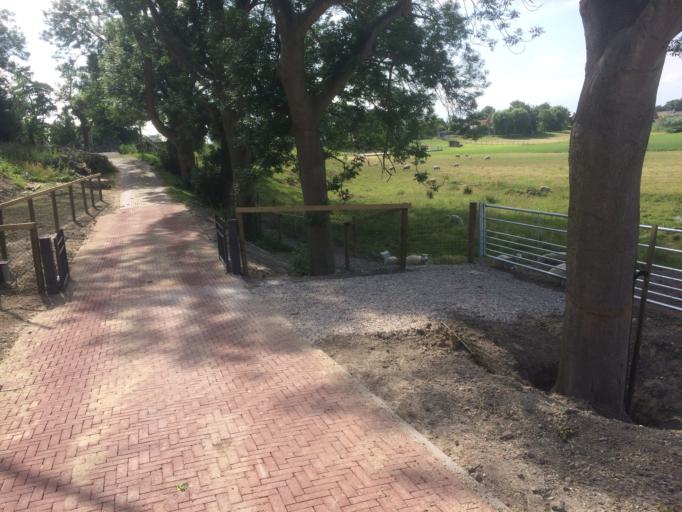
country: NL
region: South Holland
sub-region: Gemeente Kaag en Braassem
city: Leimuiden
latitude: 52.1913
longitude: 4.6774
